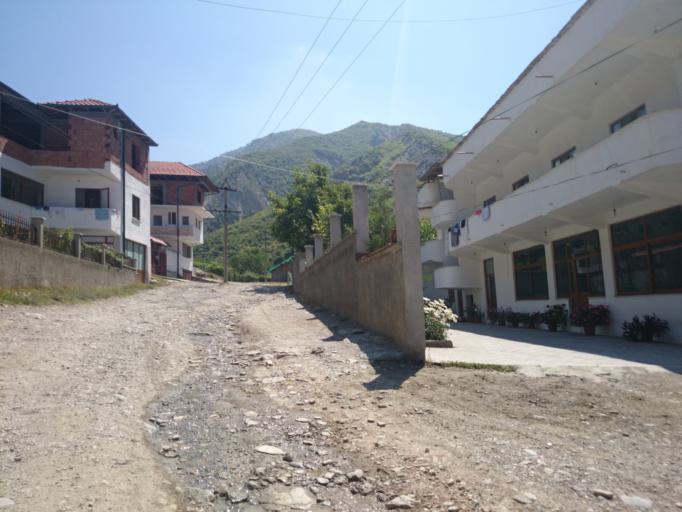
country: AL
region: Diber
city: Peshkopi
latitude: 41.6854
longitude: 20.4509
